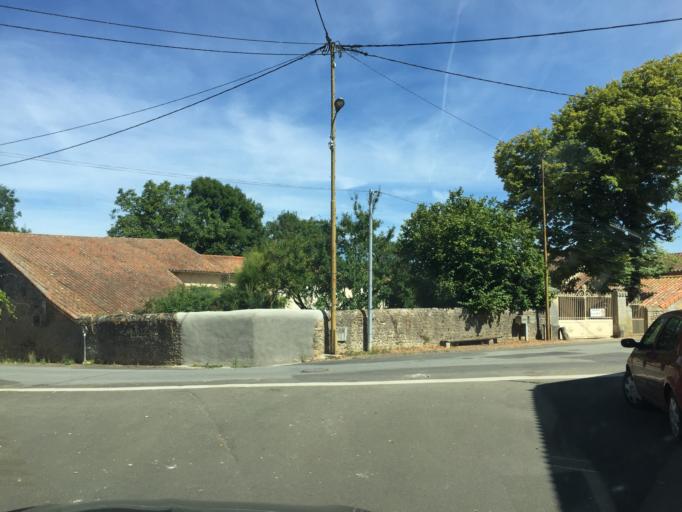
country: FR
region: Poitou-Charentes
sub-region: Departement de la Vienne
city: La Villedieu-du-Clain
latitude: 46.4439
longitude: 0.3338
